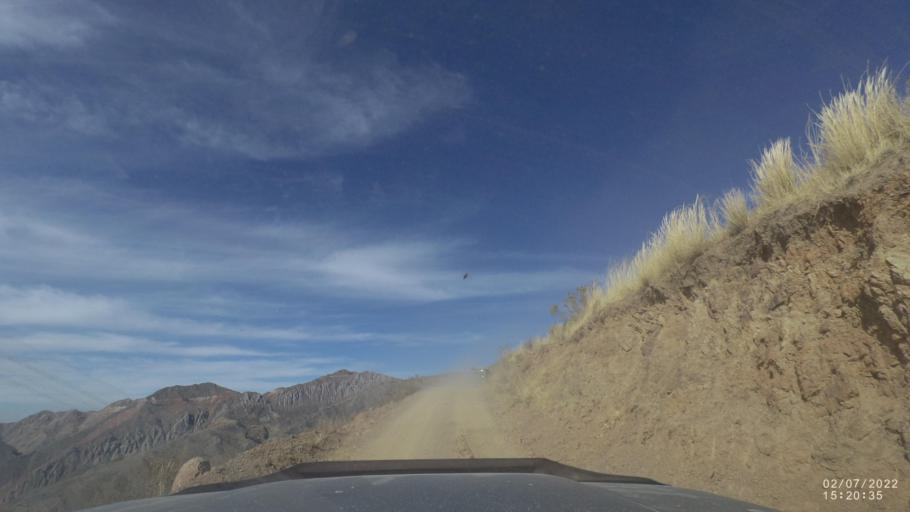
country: BO
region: Cochabamba
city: Irpa Irpa
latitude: -17.8700
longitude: -66.4269
